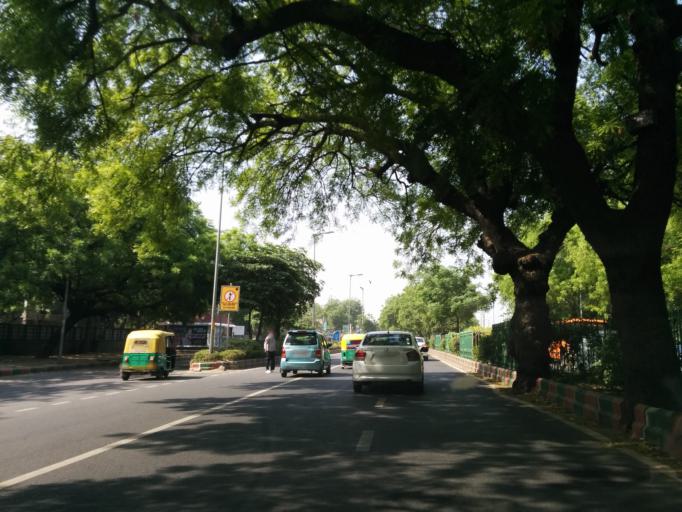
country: IN
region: NCT
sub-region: New Delhi
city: New Delhi
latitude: 28.5773
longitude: 77.2106
